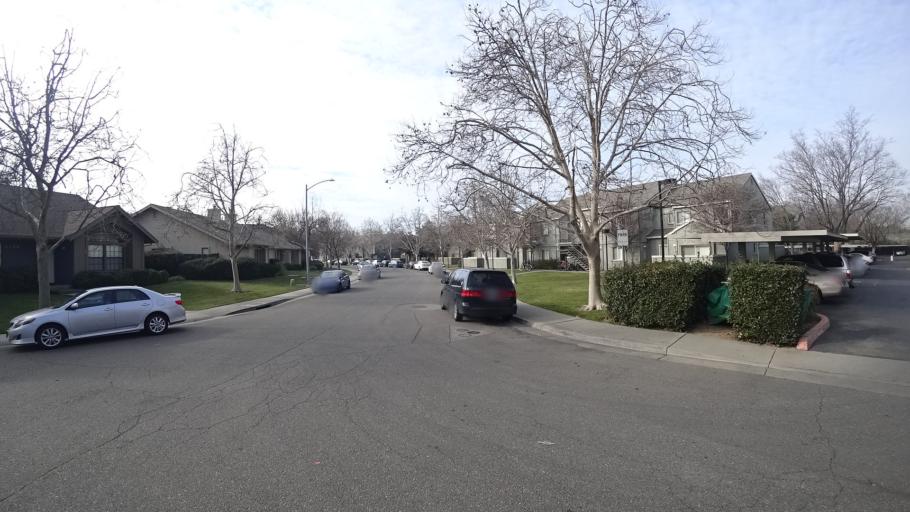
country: US
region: California
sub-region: Yolo County
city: Davis
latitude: 38.5390
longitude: -121.7219
